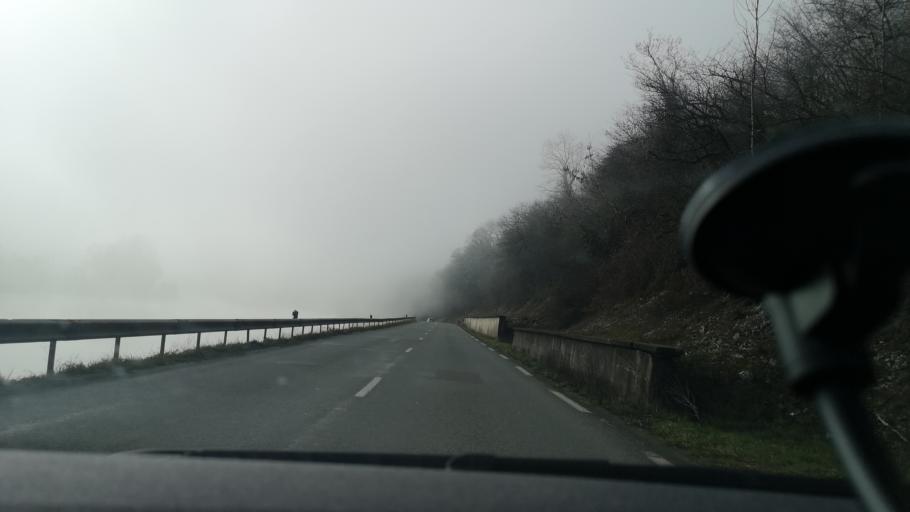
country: FR
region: Franche-Comte
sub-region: Departement du Doubs
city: Baume-les-Dames
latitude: 47.3697
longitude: 6.4200
